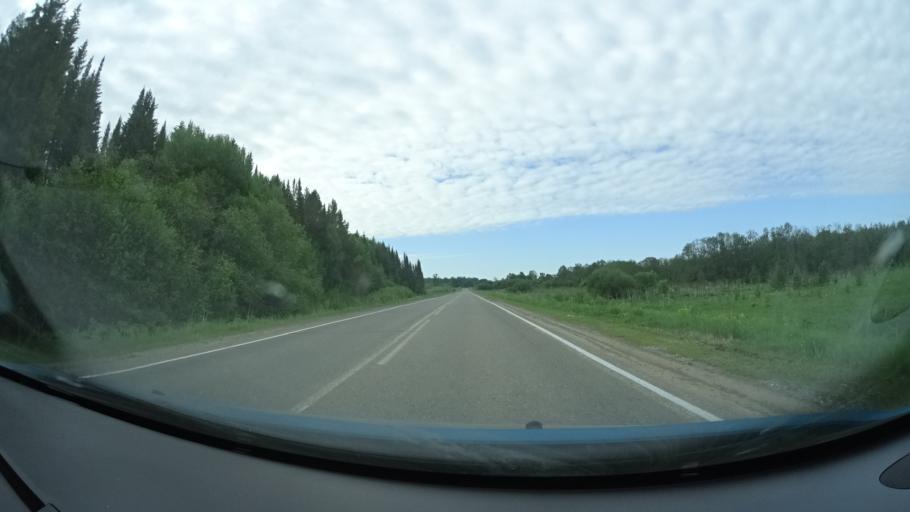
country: RU
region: Perm
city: Kuyeda
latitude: 56.5150
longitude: 55.6261
